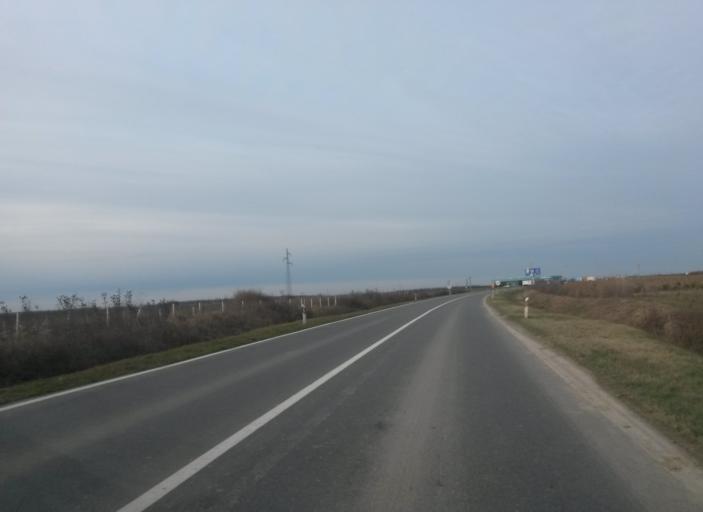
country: HR
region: Osjecko-Baranjska
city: Ovcara
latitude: 45.5088
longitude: 18.5416
